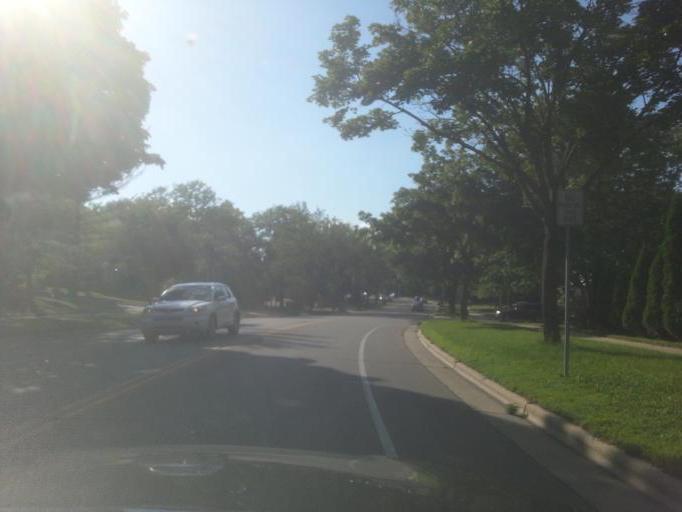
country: US
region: Wisconsin
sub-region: Dane County
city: Middleton
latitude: 43.0754
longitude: -89.4995
